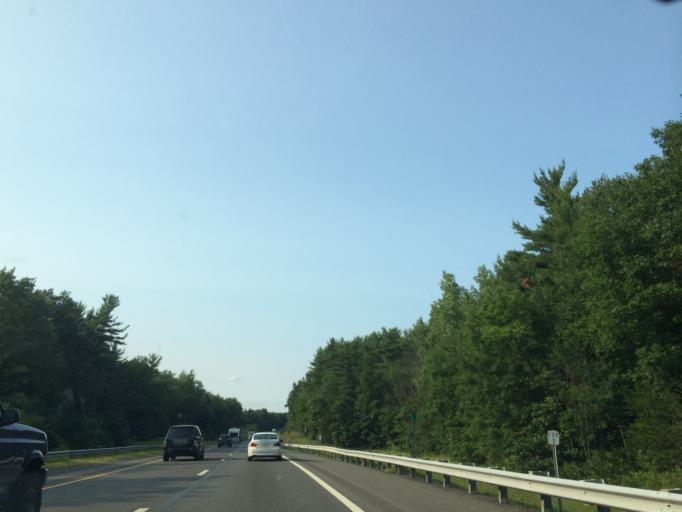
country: US
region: New York
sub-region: Greene County
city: Coxsackie
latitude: 42.3375
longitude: -73.8585
